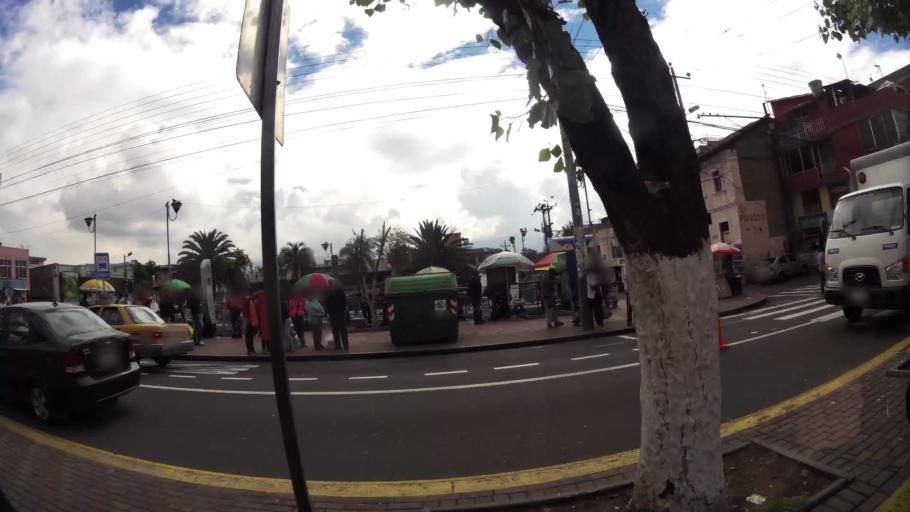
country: EC
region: Pichincha
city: Sangolqui
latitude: -0.3272
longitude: -78.4502
